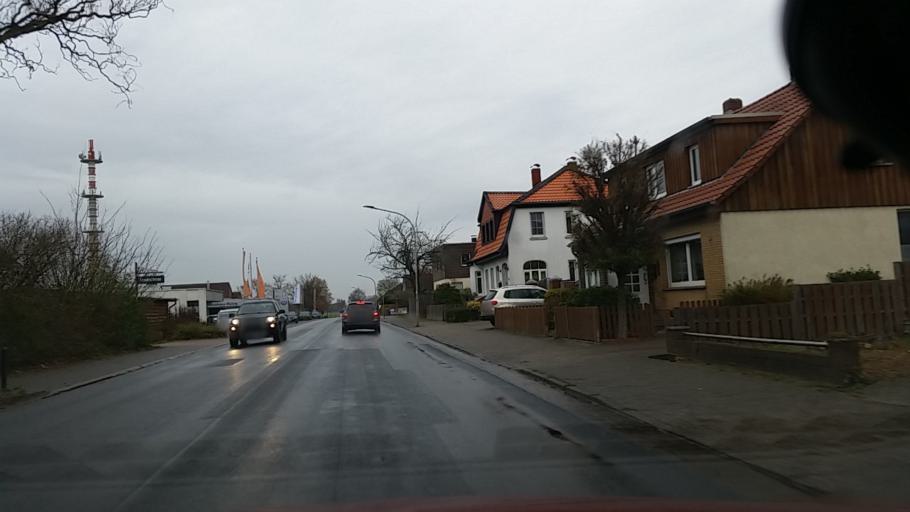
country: DE
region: Lower Saxony
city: Wittingen
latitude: 52.7337
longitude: 10.7371
